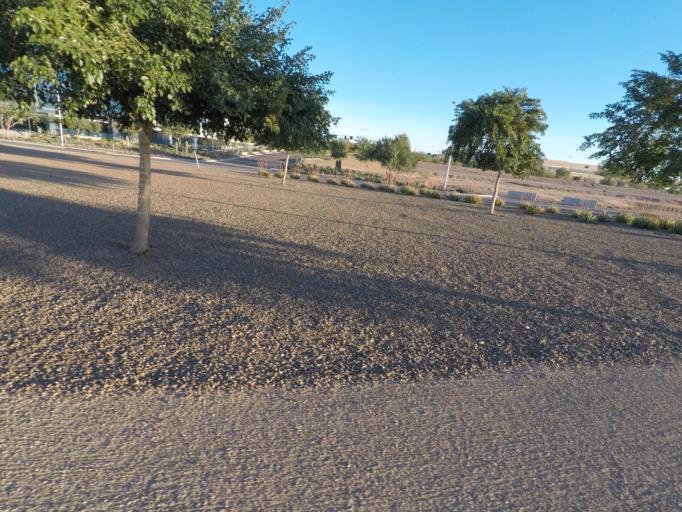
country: US
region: Arizona
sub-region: Maricopa County
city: Tempe Junction
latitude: 33.4392
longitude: -111.9552
